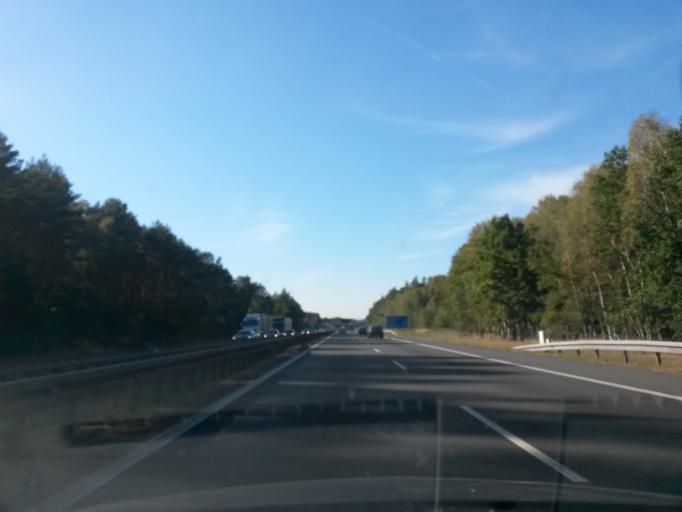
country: PL
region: Opole Voivodeship
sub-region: Powiat opolski
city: Dabrowa
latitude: 50.6638
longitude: 17.6895
